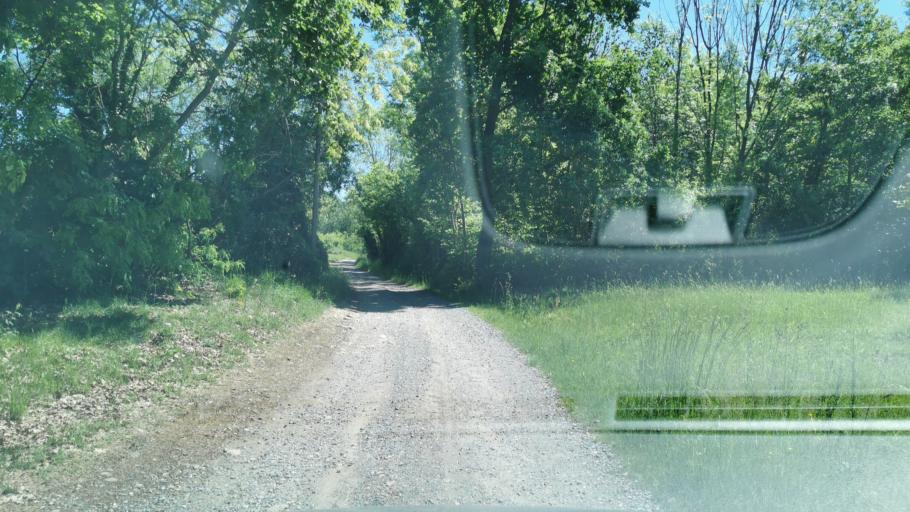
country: IT
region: Piedmont
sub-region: Provincia di Torino
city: Barbania
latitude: 45.2835
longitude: 7.6479
